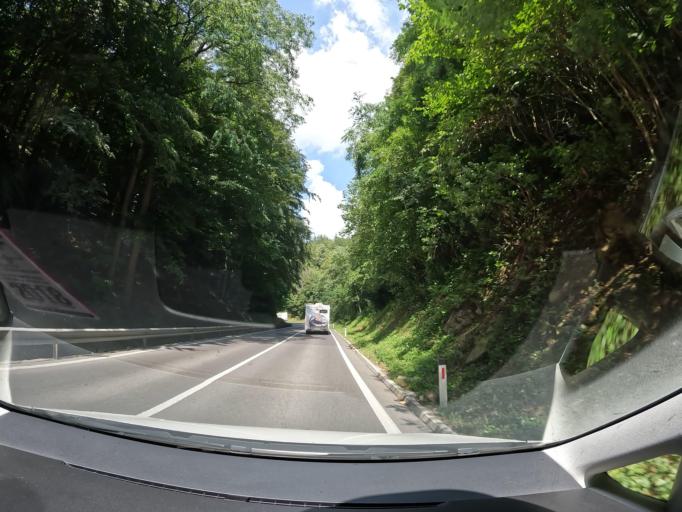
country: SI
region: Ilirska Bistrica
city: Ilirska Bistrica
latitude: 45.5139
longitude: 14.2538
